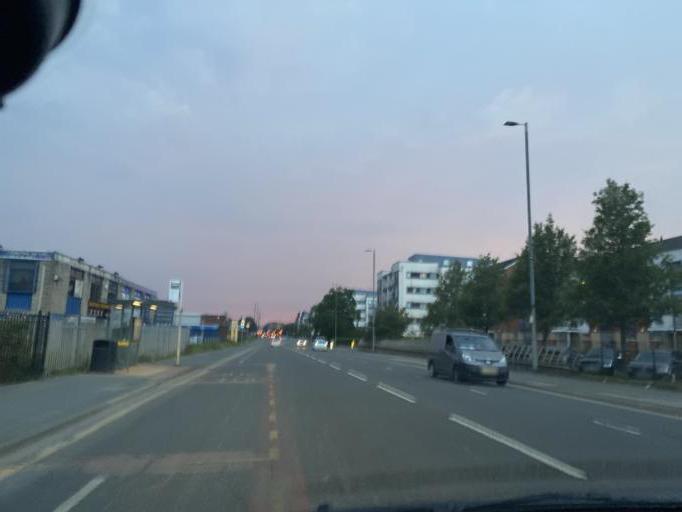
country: GB
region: England
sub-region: Manchester
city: Longsight
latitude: 53.4743
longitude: -2.1994
